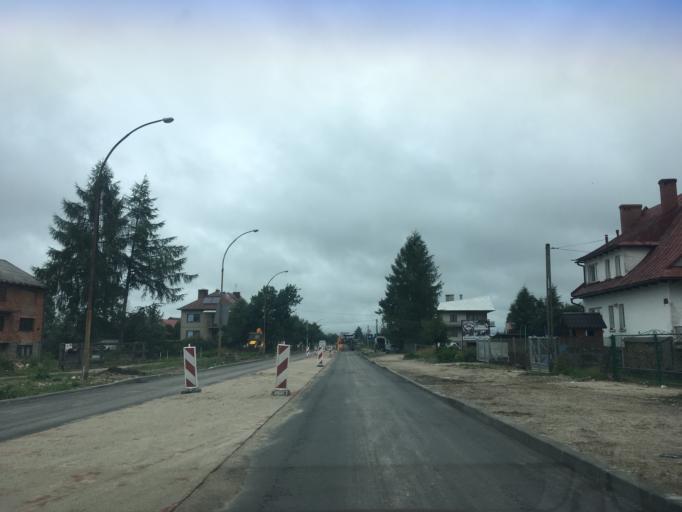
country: PL
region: Lesser Poland Voivodeship
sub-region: Powiat nowotarski
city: Czarny Dunajec
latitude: 49.4425
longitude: 19.8524
